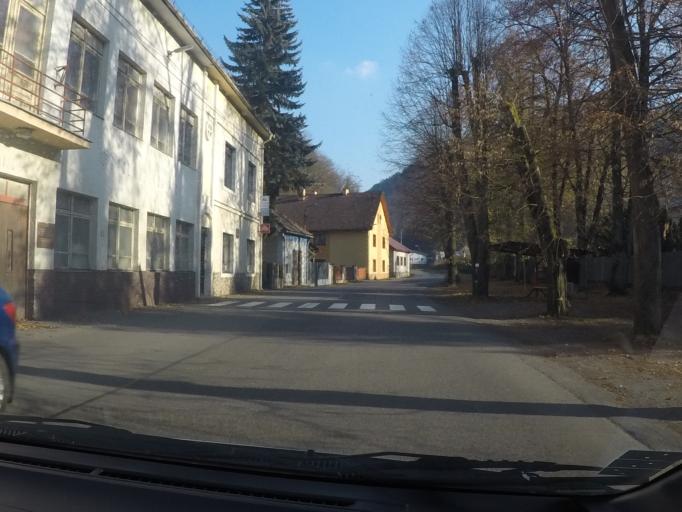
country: SK
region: Banskobystricky
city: Zarnovica
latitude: 48.4558
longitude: 18.7713
